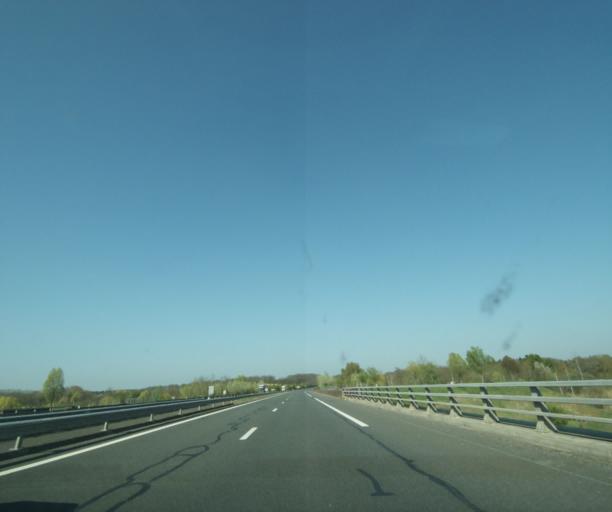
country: FR
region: Centre
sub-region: Departement du Loiret
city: Dordives
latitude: 48.1568
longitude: 2.7547
